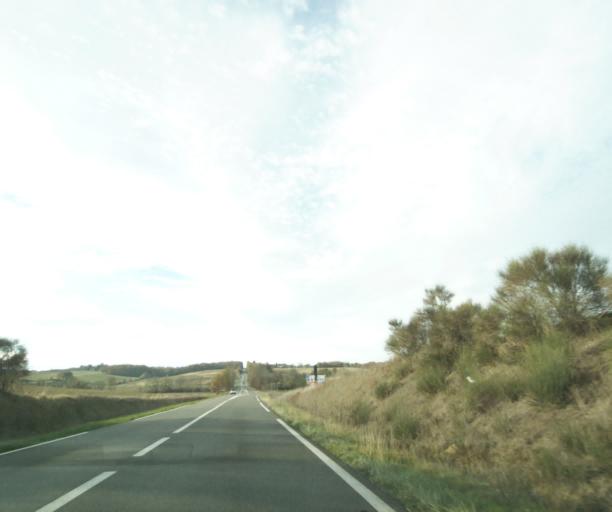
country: FR
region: Midi-Pyrenees
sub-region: Departement du Gers
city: Vic-Fezensac
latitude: 43.7516
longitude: 0.2669
